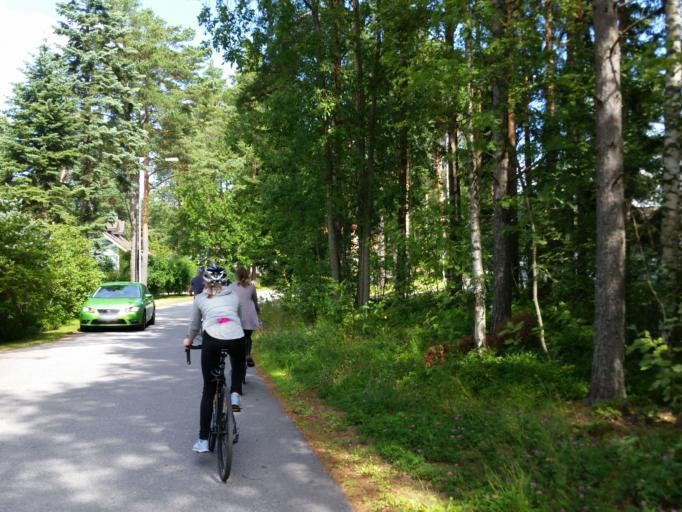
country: FI
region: Uusimaa
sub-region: Raaseporin
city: Hanko
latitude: 59.8435
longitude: 22.9353
